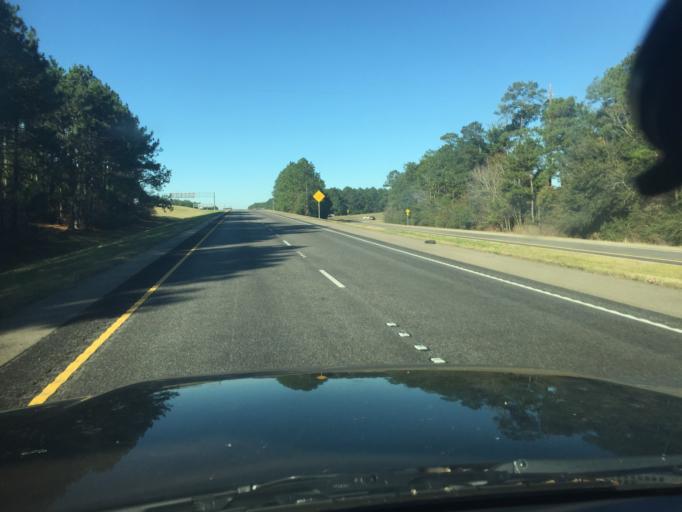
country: US
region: Louisiana
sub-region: Saint Tammany Parish
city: Slidell
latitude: 30.3051
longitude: -89.7368
